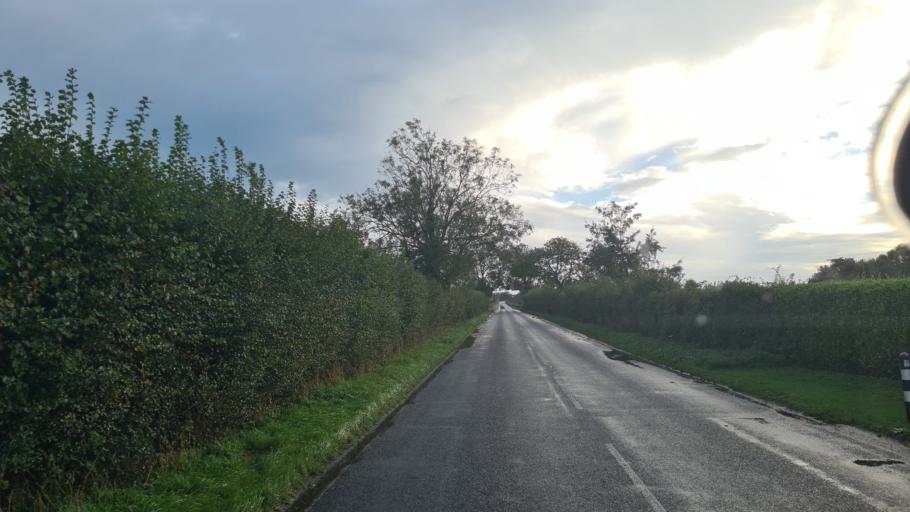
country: GB
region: England
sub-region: West Sussex
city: Arundel
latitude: 50.8370
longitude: -0.5739
